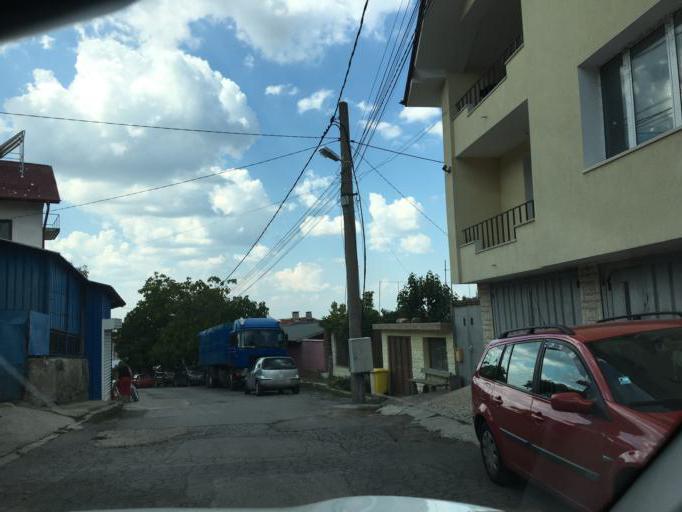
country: BG
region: Sofiya
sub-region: Obshtina Elin Pelin
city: Elin Pelin
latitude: 42.5994
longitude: 23.4798
